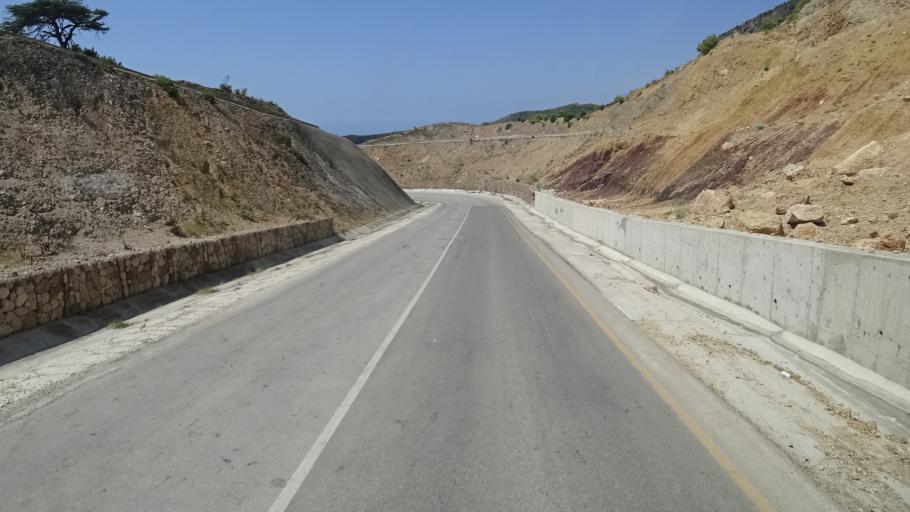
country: OM
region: Zufar
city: Salalah
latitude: 17.0486
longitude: 54.6113
